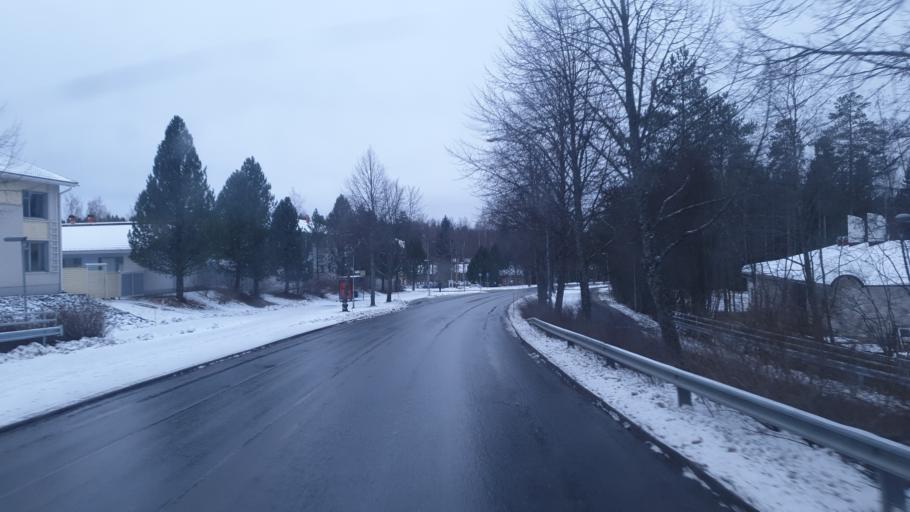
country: FI
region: Northern Savo
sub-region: Kuopio
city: Kuopio
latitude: 62.8372
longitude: 27.6344
